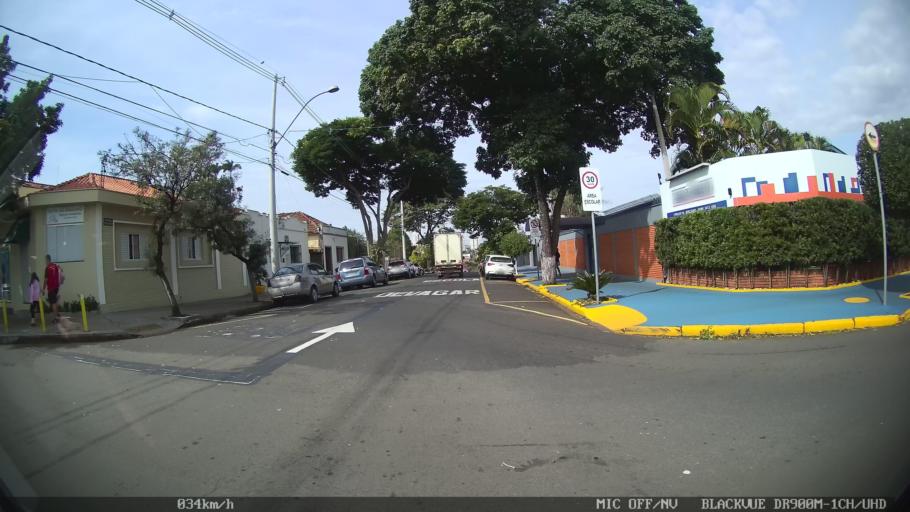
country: BR
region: Sao Paulo
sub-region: Piracicaba
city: Piracicaba
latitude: -22.7152
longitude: -47.6562
